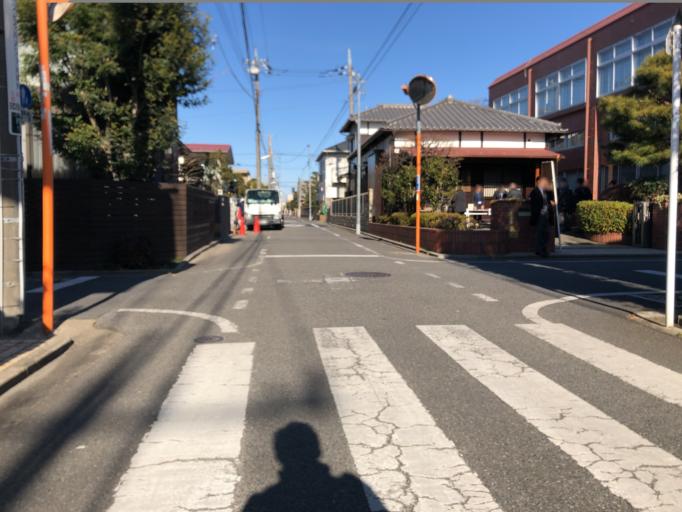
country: JP
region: Tokyo
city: Musashino
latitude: 35.7059
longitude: 139.5574
